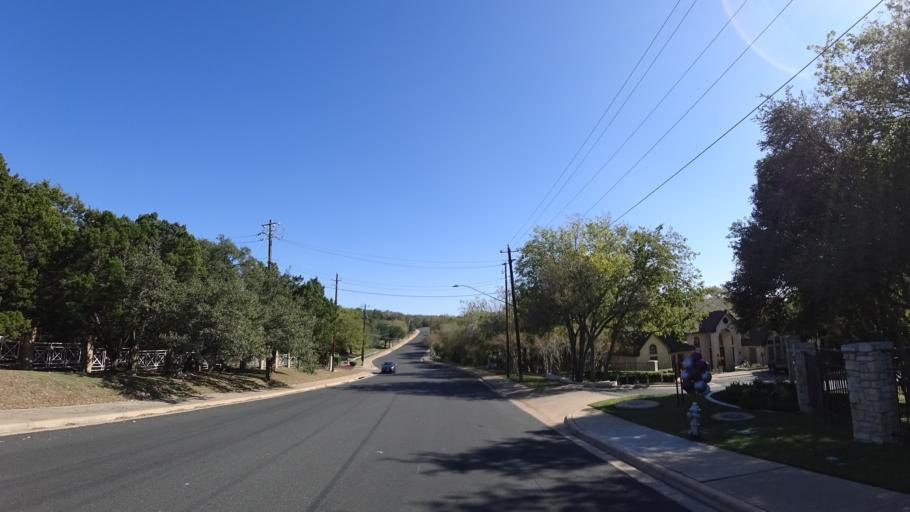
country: US
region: Texas
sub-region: Williamson County
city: Jollyville
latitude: 30.4107
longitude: -97.7527
